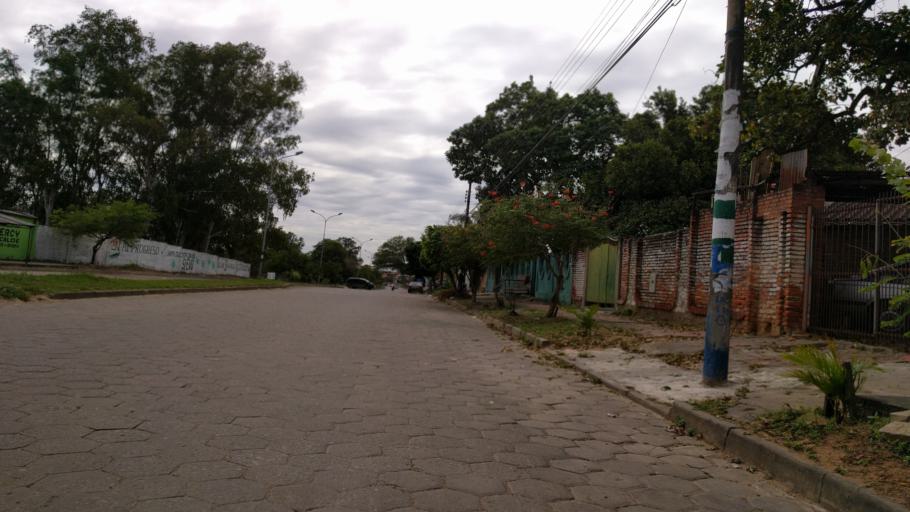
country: BO
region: Santa Cruz
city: Santa Cruz de la Sierra
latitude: -17.8146
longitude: -63.1976
